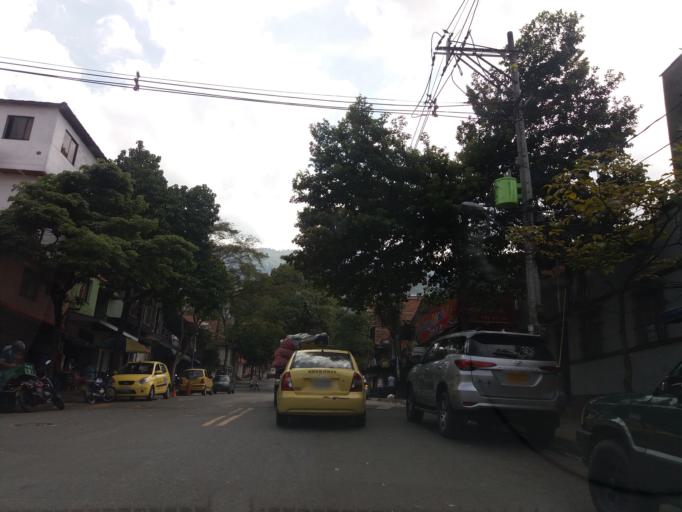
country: CO
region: Antioquia
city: Medellin
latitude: 6.2834
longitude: -75.5598
